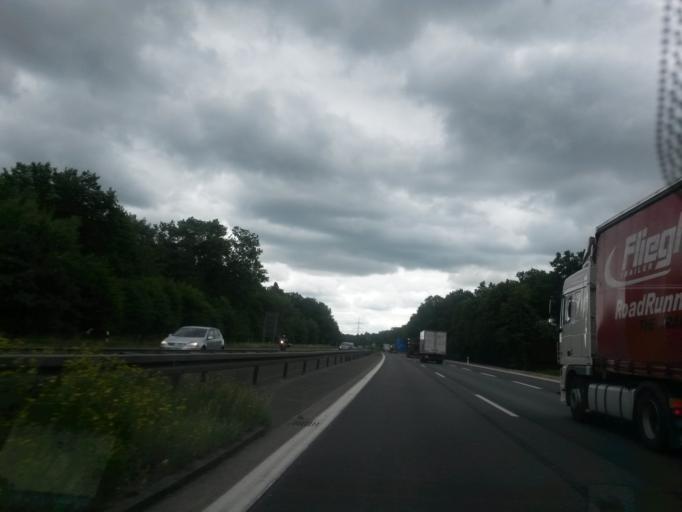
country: DE
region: Bavaria
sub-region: Regierungsbezirk Mittelfranken
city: Herzogenaurach
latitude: 49.5768
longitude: 10.9312
